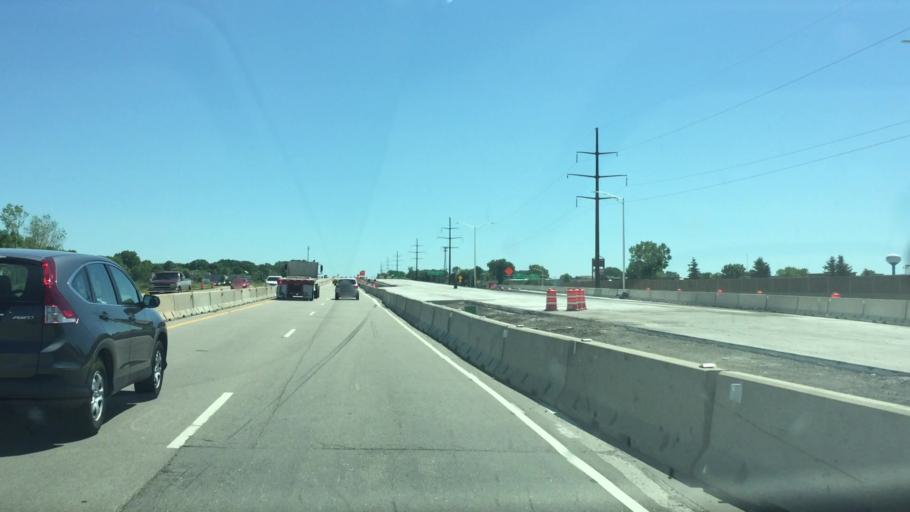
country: US
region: Wisconsin
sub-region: Outagamie County
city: Appleton
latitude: 44.2340
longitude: -88.4301
